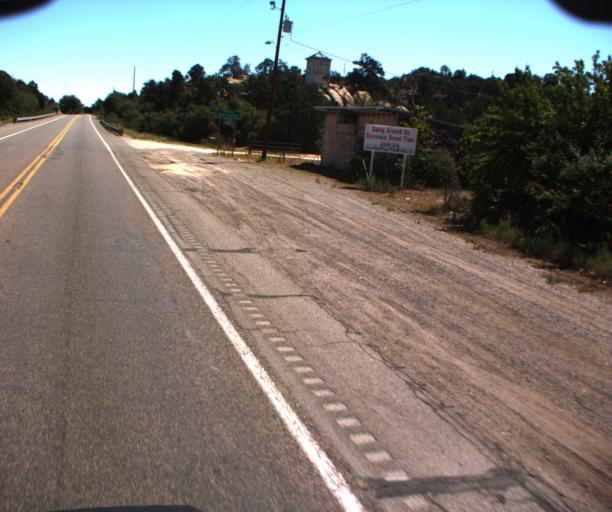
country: US
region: Arizona
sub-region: Gila County
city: Miami
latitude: 33.3531
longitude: -110.9843
